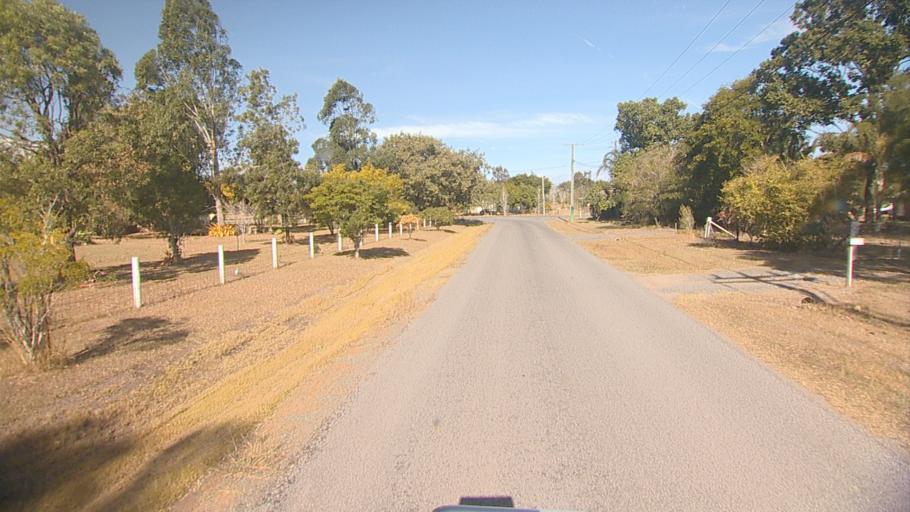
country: AU
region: Queensland
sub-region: Logan
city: Cedar Vale
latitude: -27.8670
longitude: 152.9682
